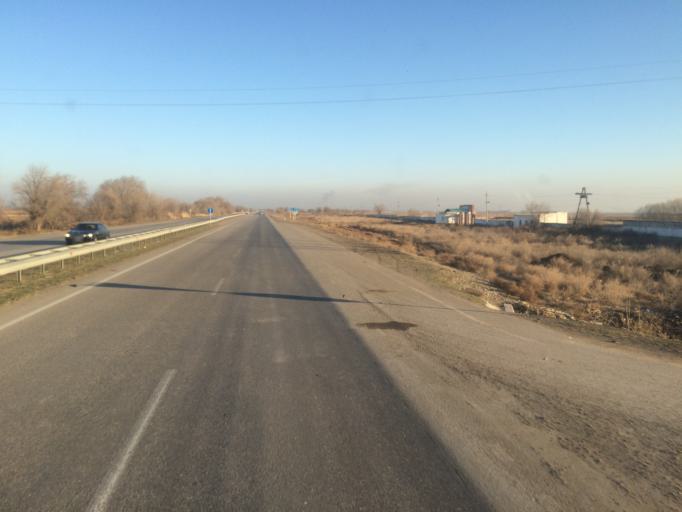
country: KZ
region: Ongtustik Qazaqstan
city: Turkestan
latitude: 43.3508
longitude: 68.1491
